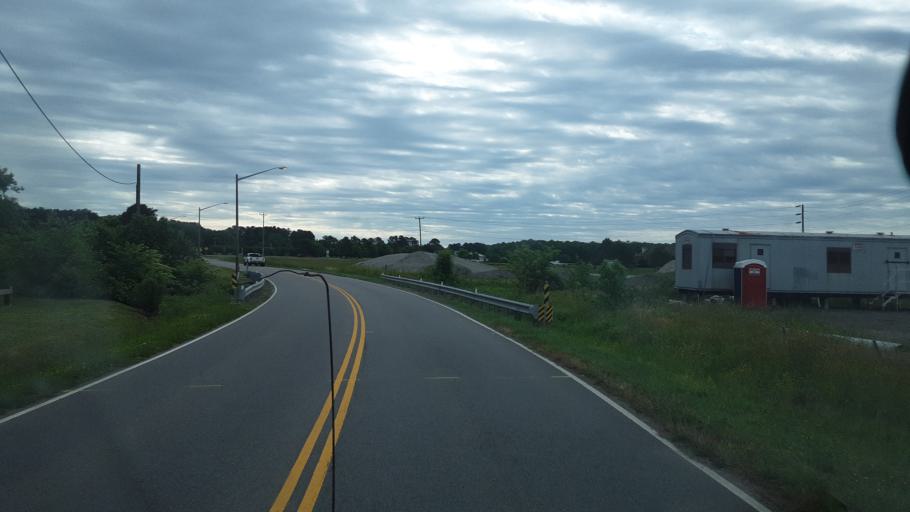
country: US
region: Virginia
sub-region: City of Virginia Beach
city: Virginia Beach
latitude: 36.7471
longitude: -76.0032
